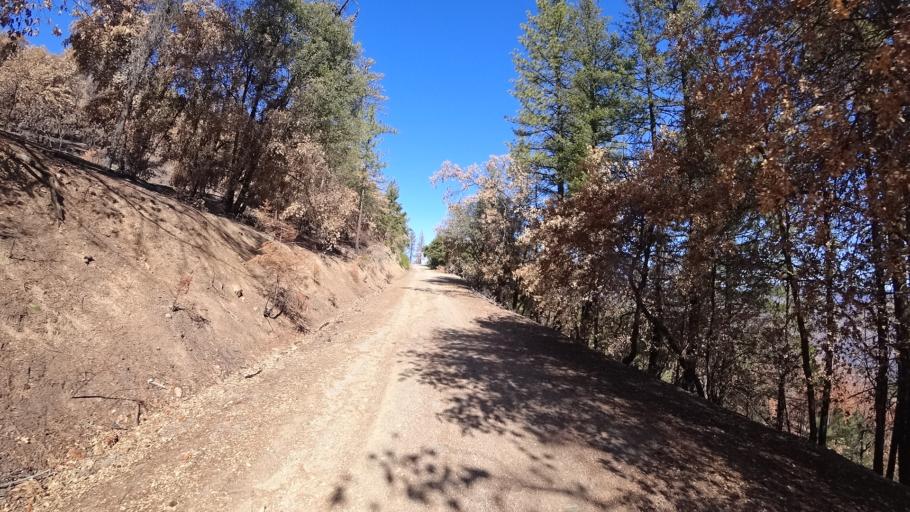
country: US
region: California
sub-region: Tehama County
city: Rancho Tehama Reserve
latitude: 39.6782
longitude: -122.7065
